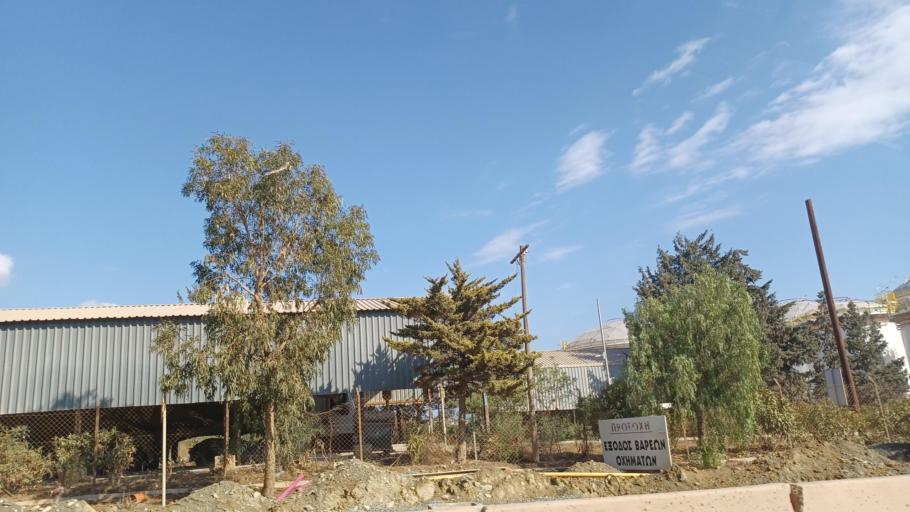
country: CY
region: Limassol
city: Pyrgos
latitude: 34.7263
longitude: 33.3087
